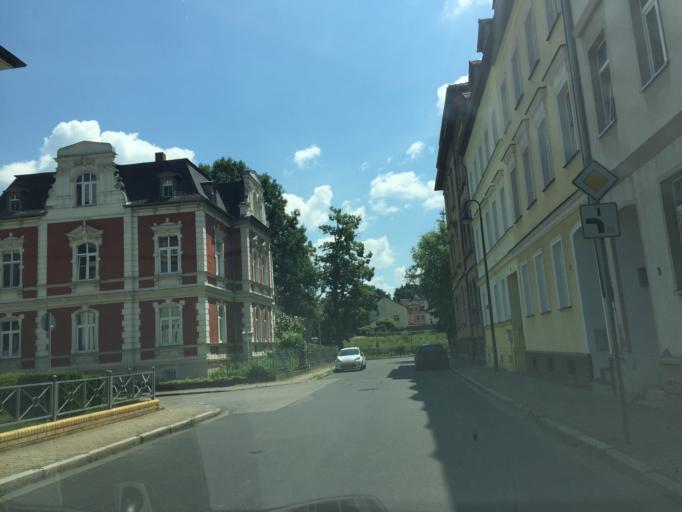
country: DE
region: Thuringia
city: Schmolln
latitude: 50.8948
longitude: 12.3472
